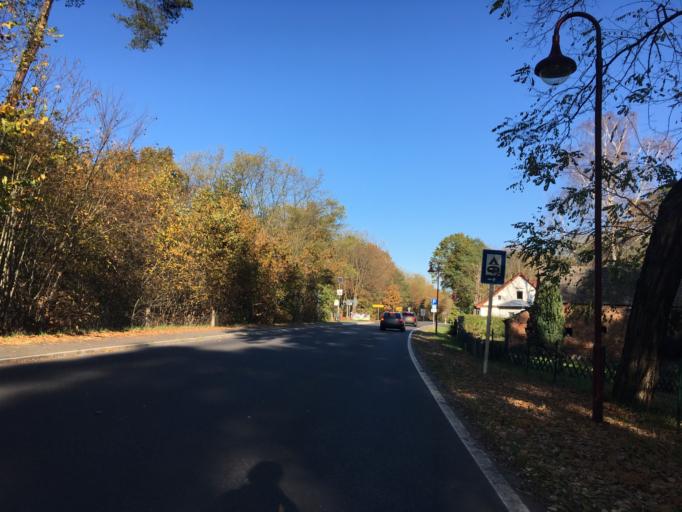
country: DE
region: Brandenburg
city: Reichenwalde
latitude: 52.2954
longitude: 13.9873
